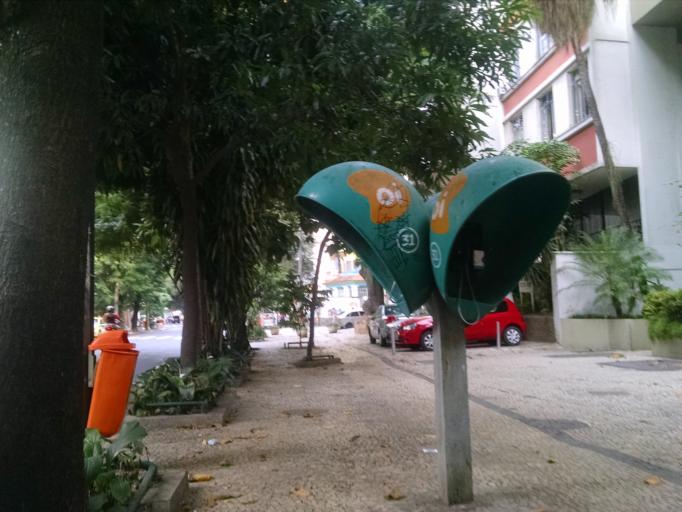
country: BR
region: Rio de Janeiro
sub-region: Rio De Janeiro
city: Rio de Janeiro
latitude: -22.9383
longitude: -43.1952
